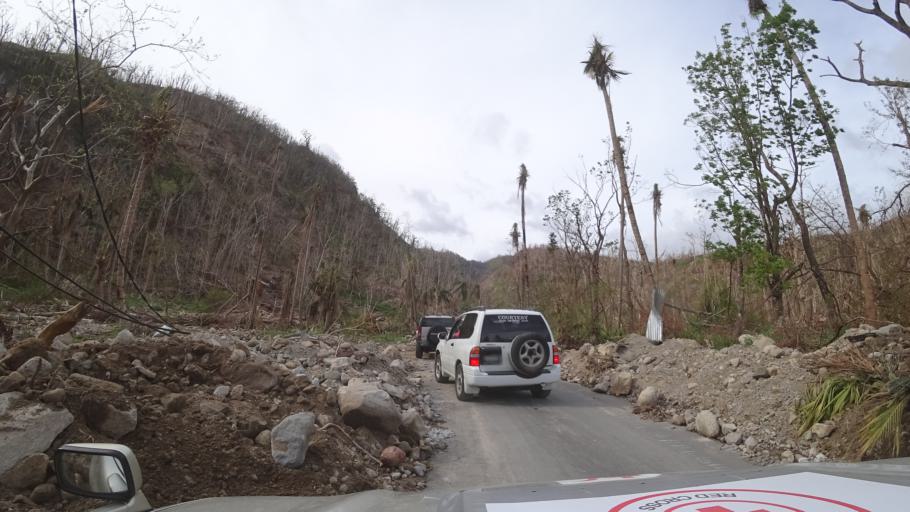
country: DM
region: Saint Patrick
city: Berekua
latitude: 15.2568
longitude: -61.3188
